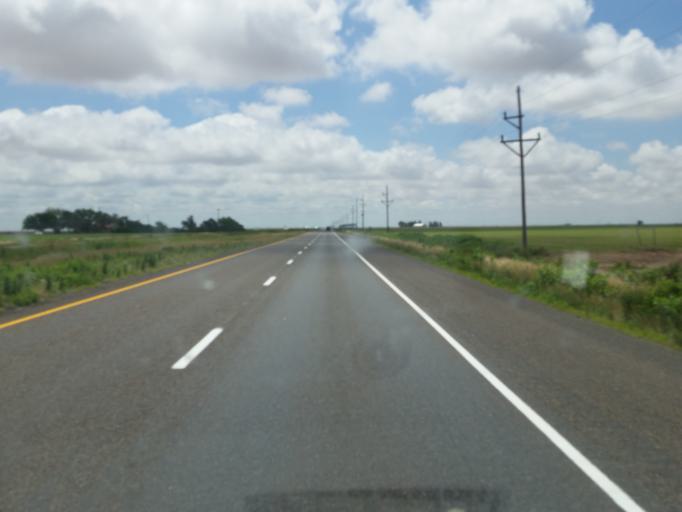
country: US
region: Texas
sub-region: Lubbock County
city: Slaton
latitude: 33.4002
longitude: -101.6131
